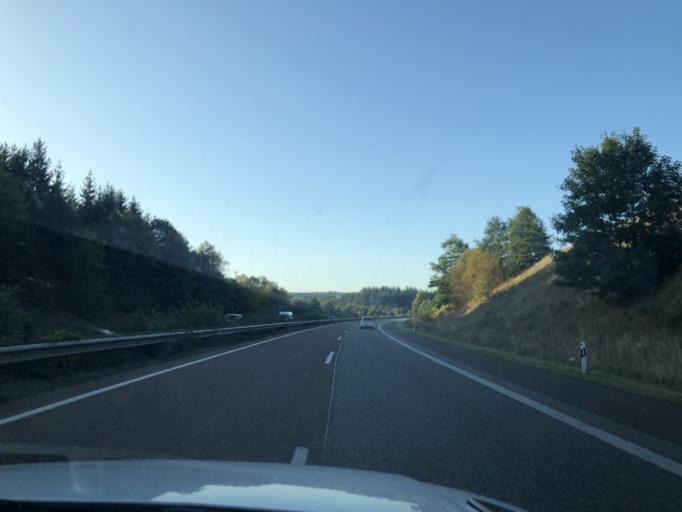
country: DE
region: Rheinland-Pfalz
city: Hermeskeil
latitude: 49.6512
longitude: 6.9266
